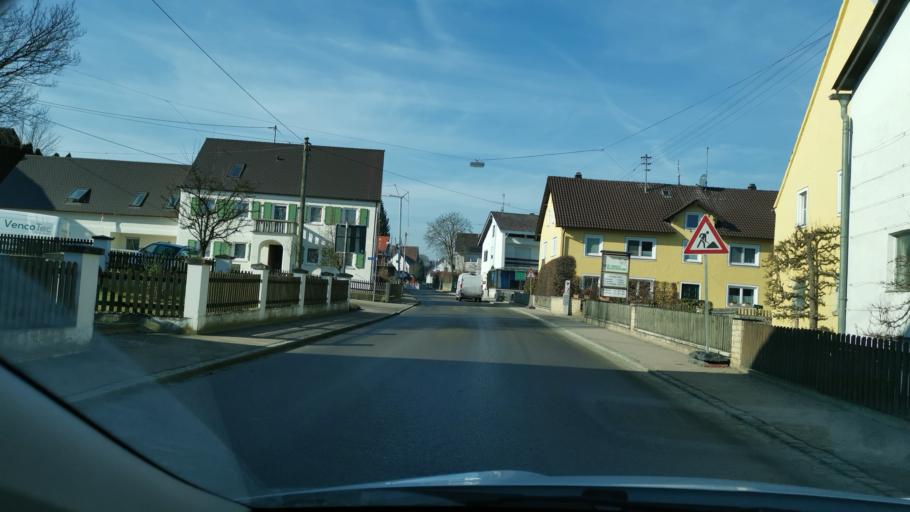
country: DE
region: Bavaria
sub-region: Swabia
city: Holzheim
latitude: 48.6130
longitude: 10.9493
